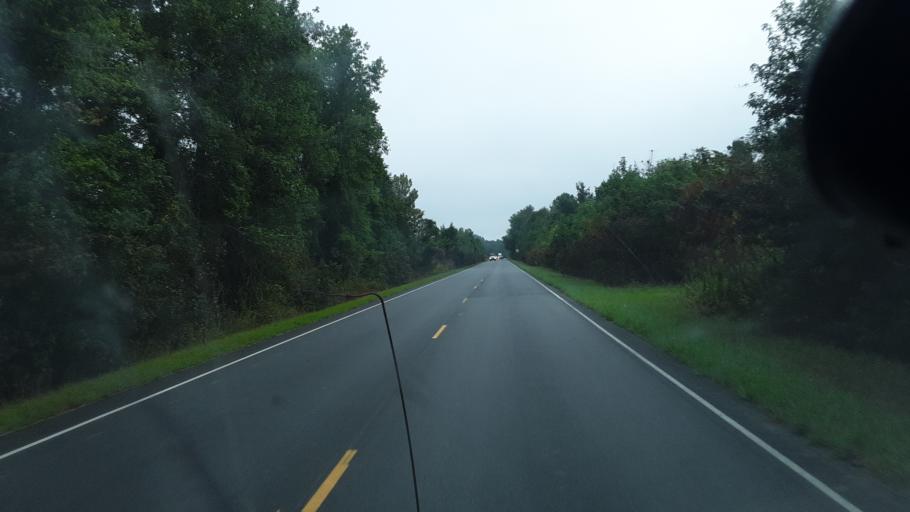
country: US
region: South Carolina
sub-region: Florence County
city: Johnsonville
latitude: 33.8966
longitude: -79.4446
